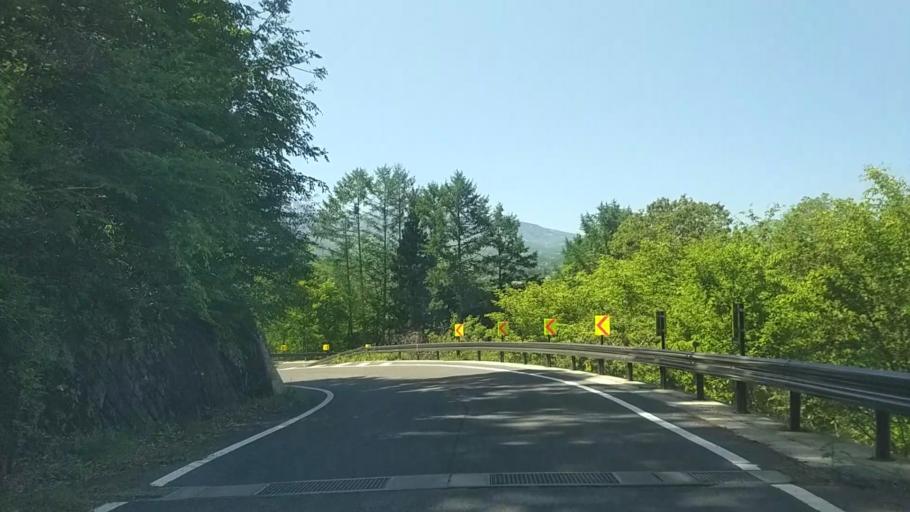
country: JP
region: Yamanashi
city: Nirasaki
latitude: 35.8713
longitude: 138.4516
